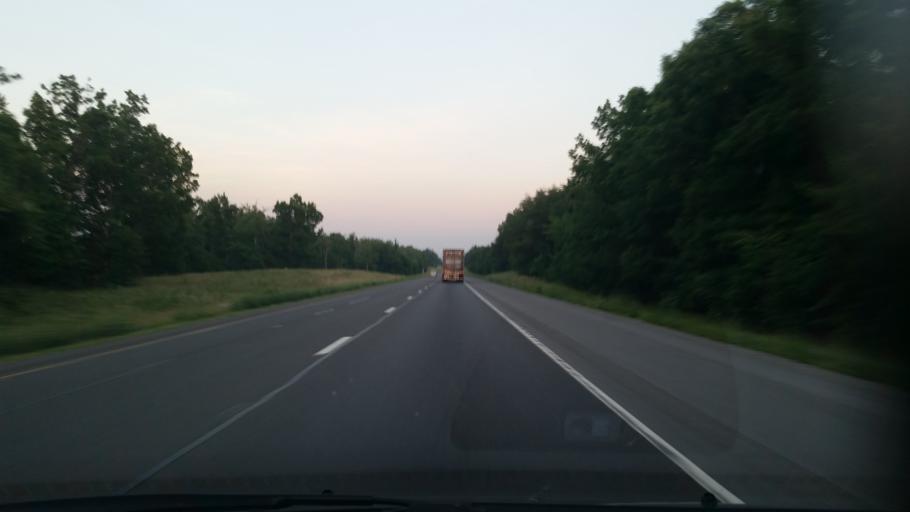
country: US
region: Tennessee
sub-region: Cumberland County
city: Crossville
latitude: 36.0295
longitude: -85.0929
